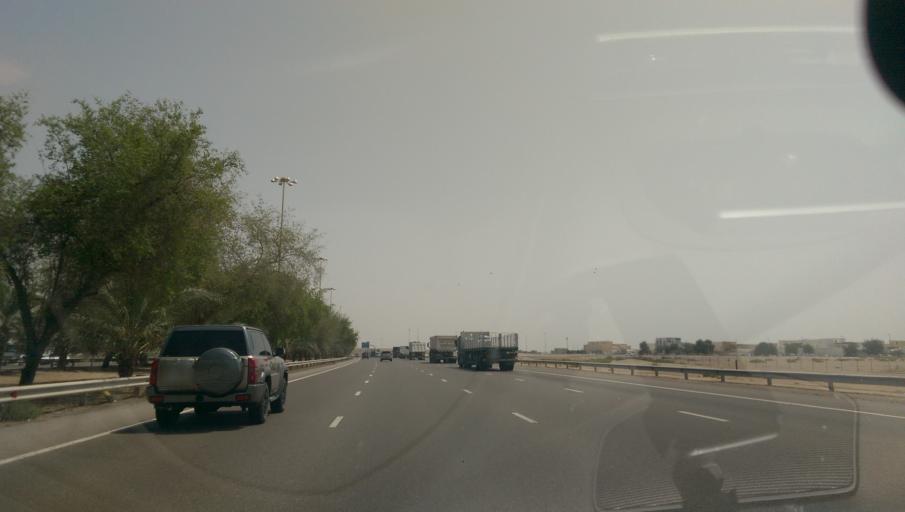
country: AE
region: Abu Dhabi
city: Abu Dhabi
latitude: 24.3611
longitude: 54.6505
